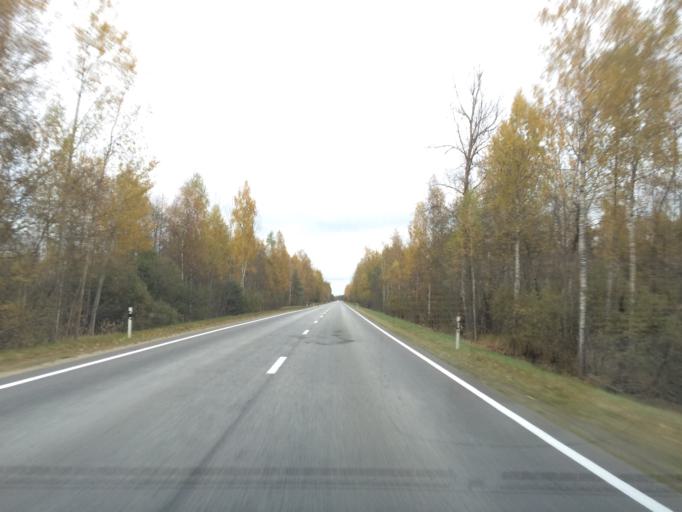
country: LV
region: Livani
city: Livani
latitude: 56.5283
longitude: 26.3958
